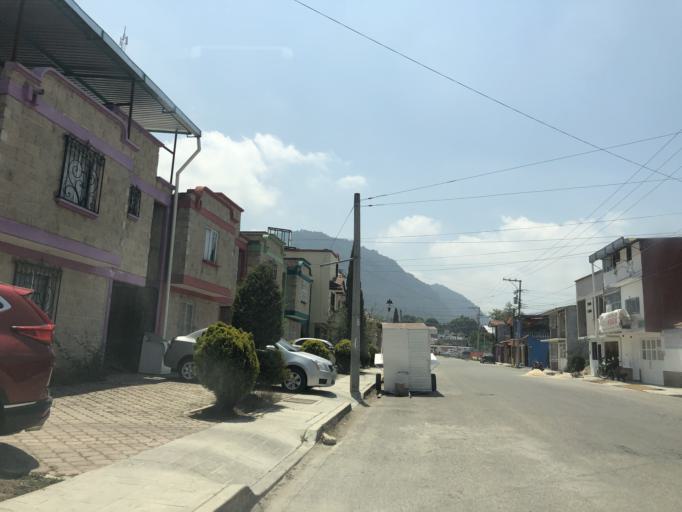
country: MX
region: Chiapas
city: San Cristobal de las Casas
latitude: 16.7165
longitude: -92.6450
